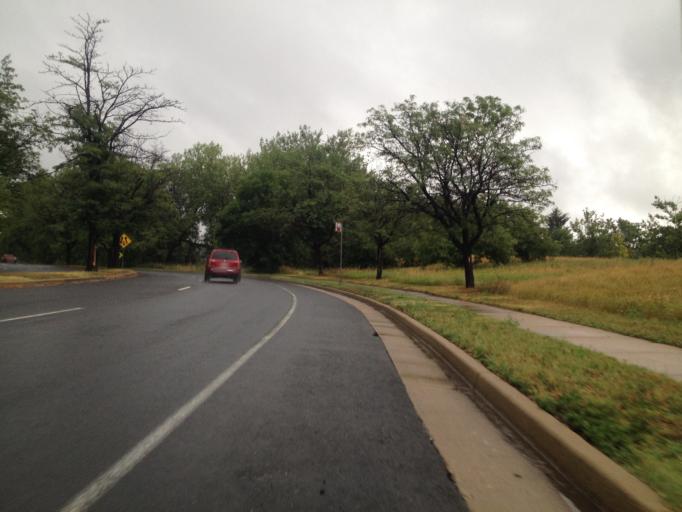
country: US
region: Colorado
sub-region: Boulder County
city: Louisville
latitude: 39.9843
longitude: -105.1439
